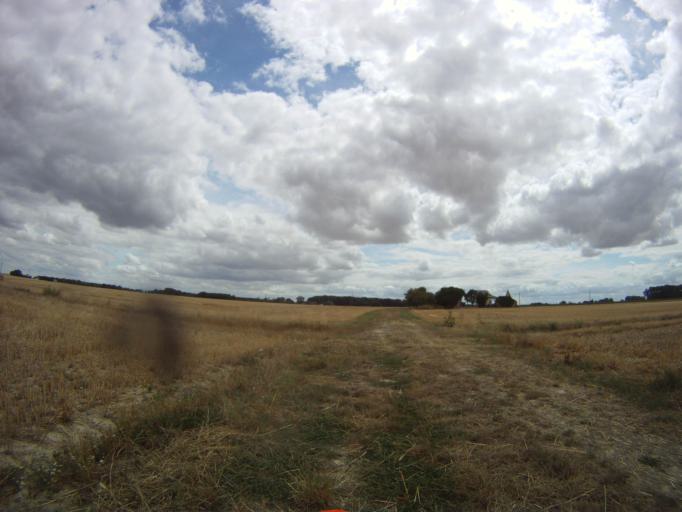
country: FR
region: Centre
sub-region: Departement du Loir-et-Cher
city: Montoire-sur-le-Loir
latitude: 47.6912
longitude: 0.8157
